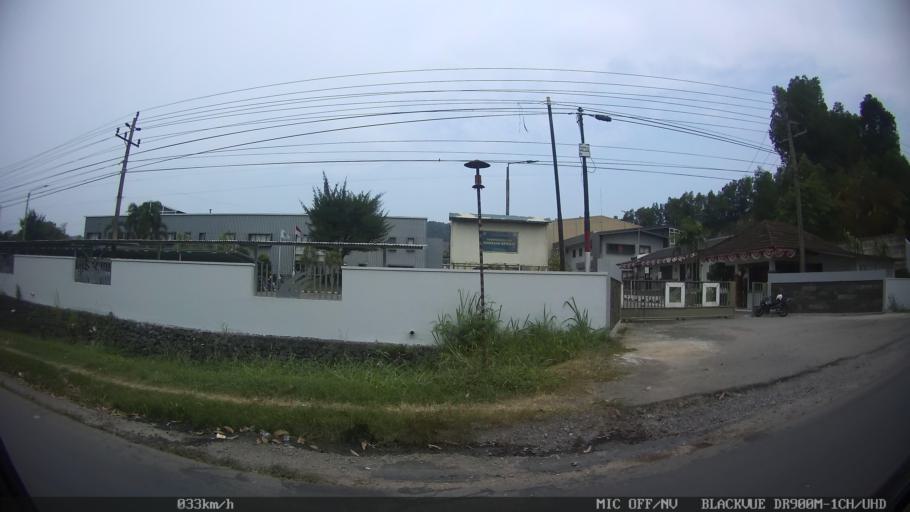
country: ID
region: Lampung
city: Panjang
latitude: -5.4154
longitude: 105.3449
